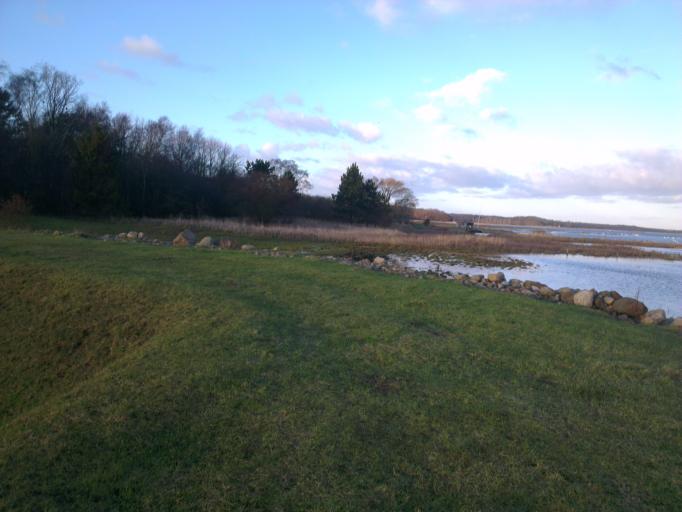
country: DK
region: Capital Region
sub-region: Frederikssund Kommune
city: Jaegerspris
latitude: 55.8687
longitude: 11.9995
